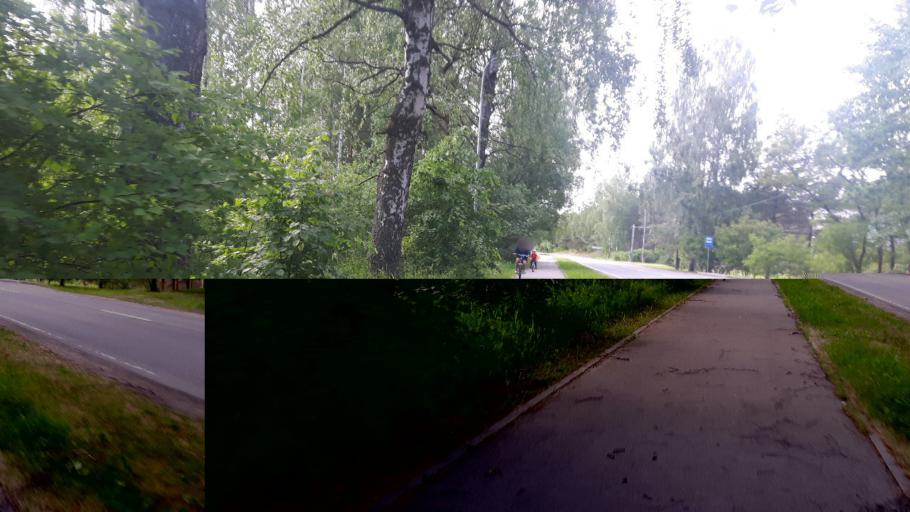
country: LV
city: Tireli
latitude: 56.9808
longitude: 23.5458
